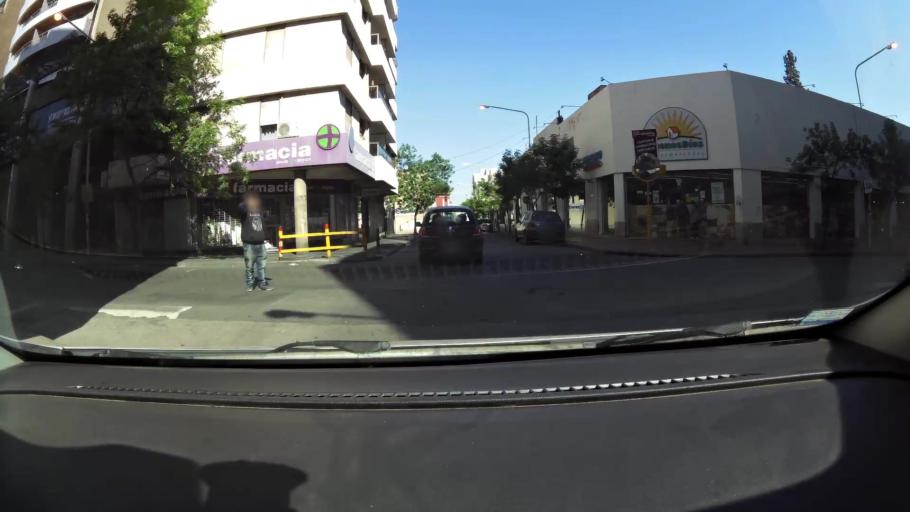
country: AR
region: Cordoba
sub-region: Departamento de Capital
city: Cordoba
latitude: -31.4228
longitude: -64.1884
